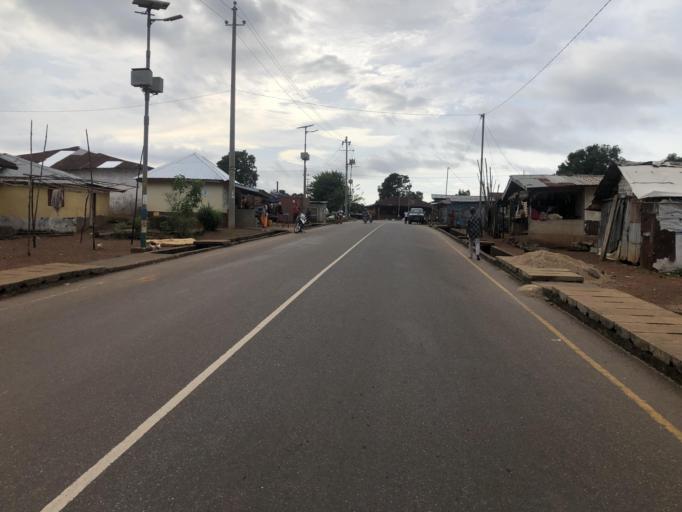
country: SL
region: Northern Province
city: Port Loko
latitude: 8.7708
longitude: -12.7885
